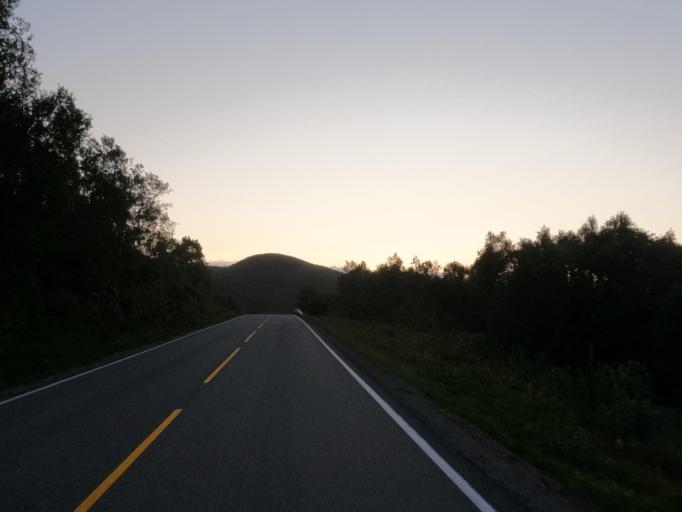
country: NO
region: Nordland
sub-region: Lodingen
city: Lodingen
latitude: 68.5180
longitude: 15.8655
